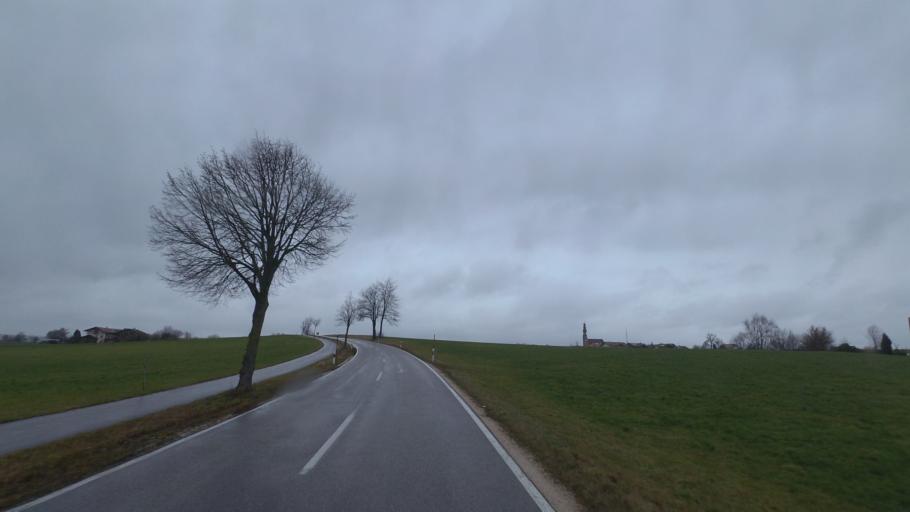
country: DE
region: Bavaria
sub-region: Upper Bavaria
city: Petting
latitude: 47.9368
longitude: 12.8045
